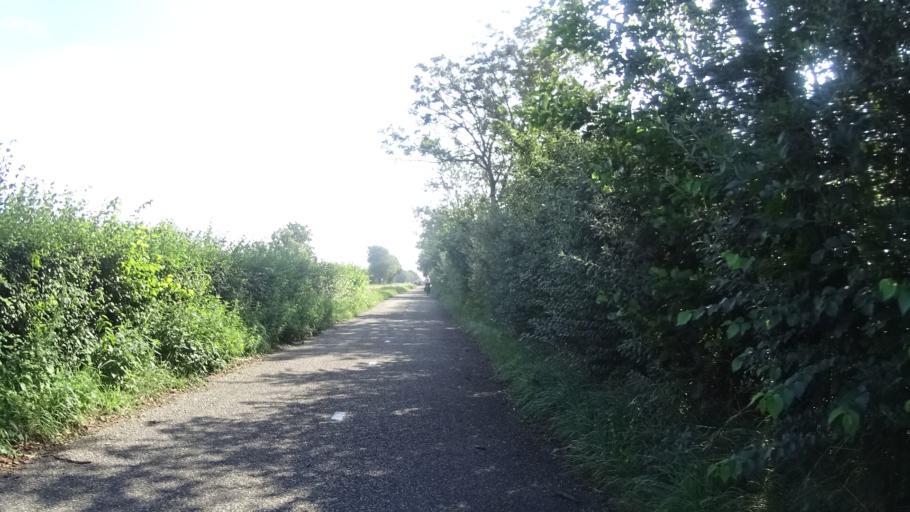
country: NL
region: Friesland
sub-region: Gemeente Franekeradeel
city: Tzum
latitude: 53.1928
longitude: 5.5951
